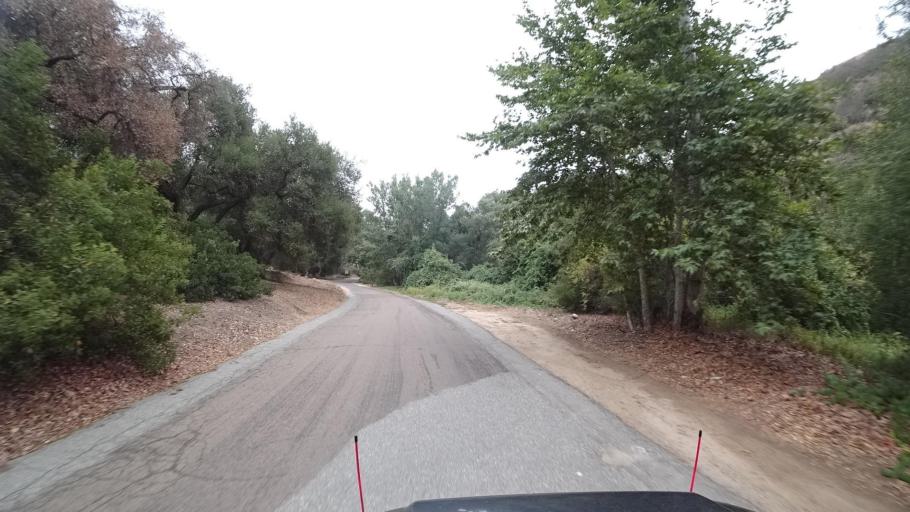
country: US
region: California
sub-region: San Diego County
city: Rainbow
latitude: 33.3755
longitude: -117.1620
